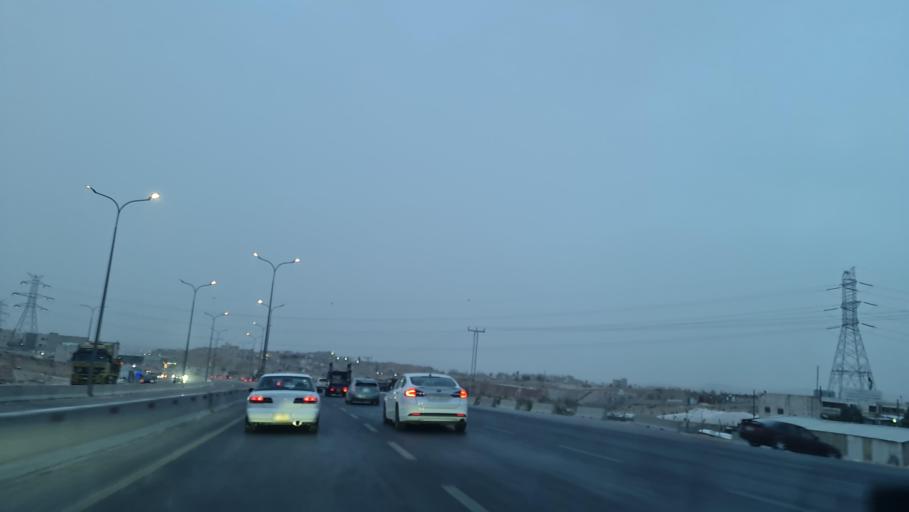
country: JO
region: Zarqa
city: Russeifa
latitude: 31.9979
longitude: 36.0328
